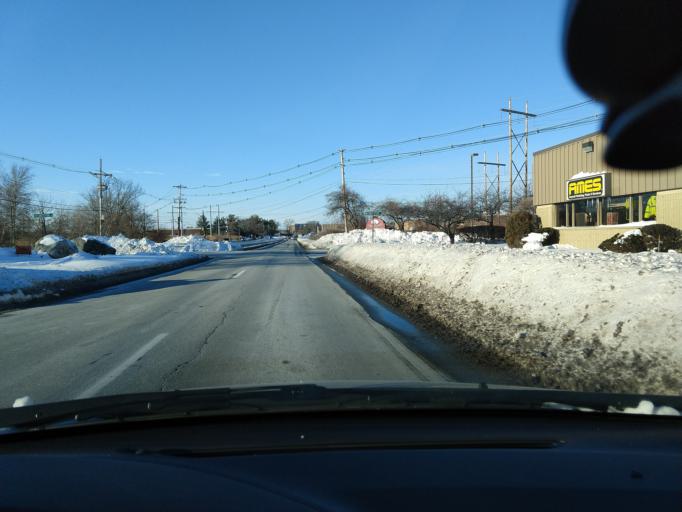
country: US
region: Massachusetts
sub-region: Middlesex County
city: Woburn
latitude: 42.5099
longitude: -71.1325
